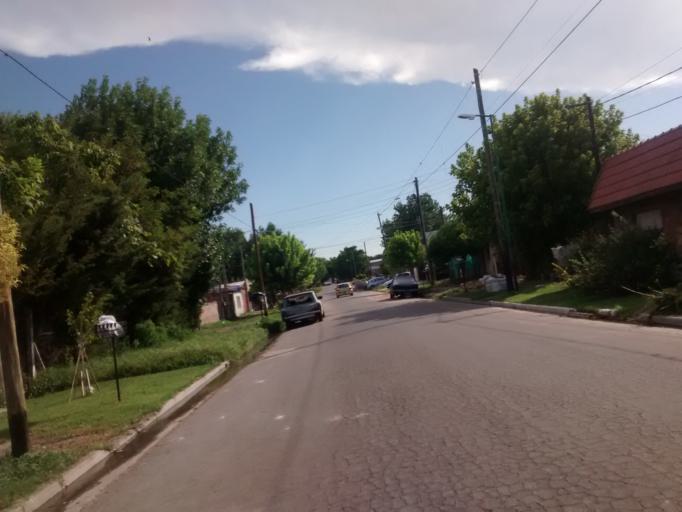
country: AR
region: Buenos Aires
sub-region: Partido de La Plata
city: La Plata
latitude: -34.9527
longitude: -57.9474
